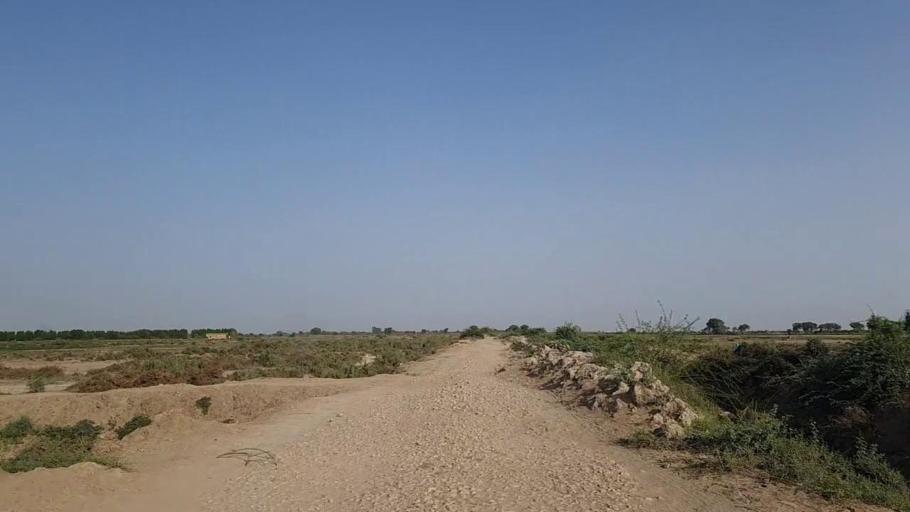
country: PK
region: Sindh
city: Jati
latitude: 24.2616
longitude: 68.1745
